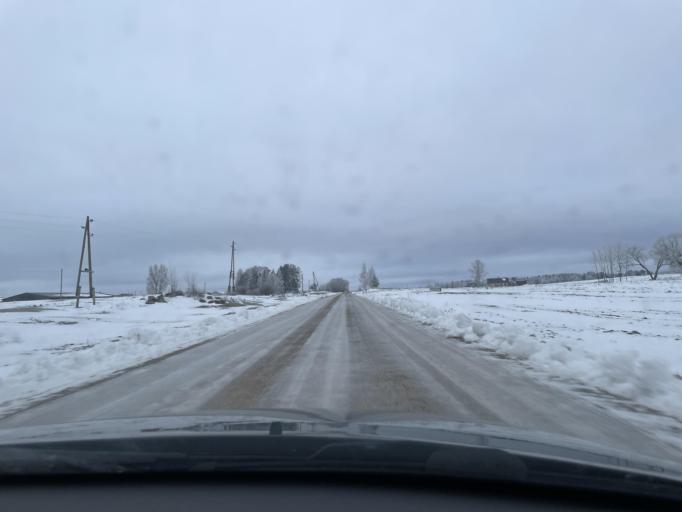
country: LV
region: Ludzas Rajons
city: Ludza
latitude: 56.4393
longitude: 27.5407
